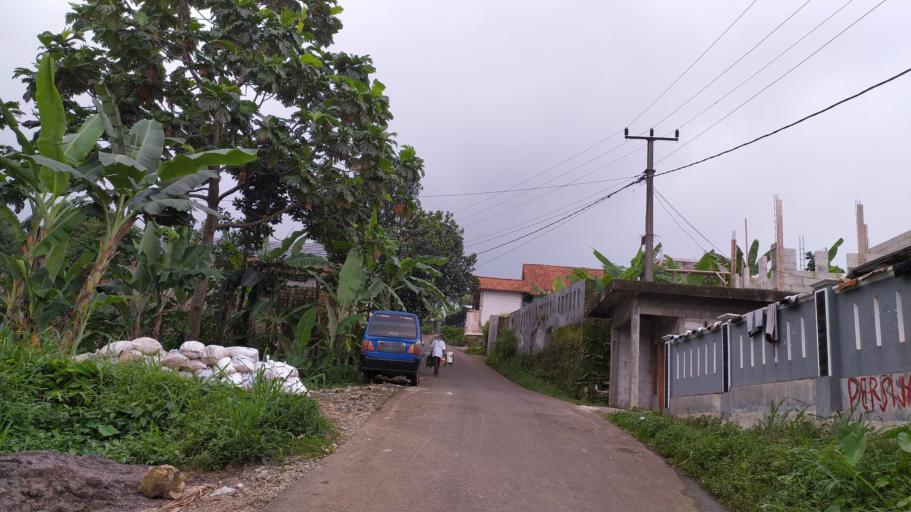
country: ID
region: West Java
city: Ciampea
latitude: -6.6369
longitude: 106.7072
